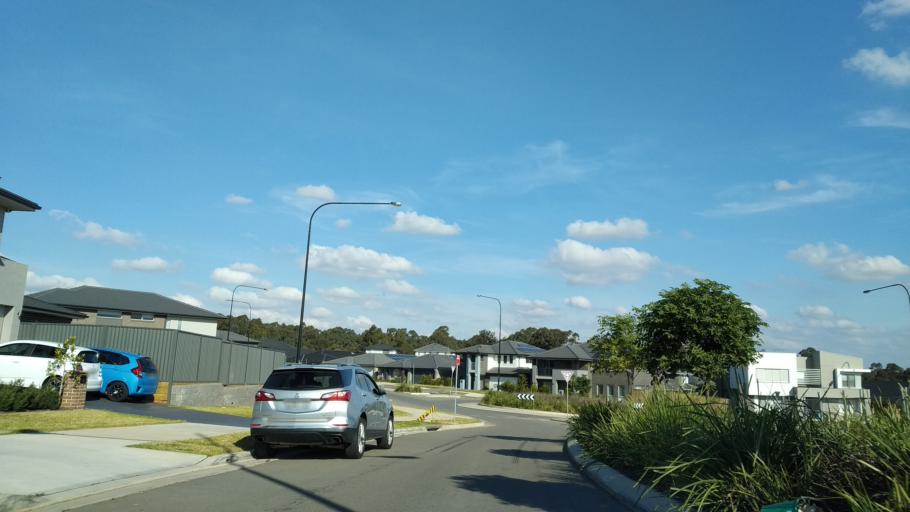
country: AU
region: New South Wales
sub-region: Blacktown
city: Hassall Grove
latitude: -33.7219
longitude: 150.8534
